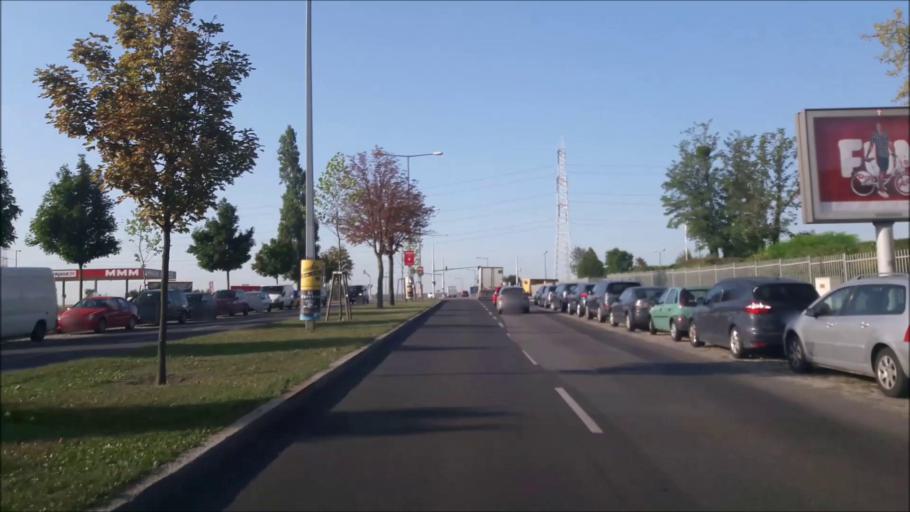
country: AT
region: Lower Austria
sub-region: Politischer Bezirk Modling
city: Vosendorf
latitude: 48.1332
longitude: 16.3558
